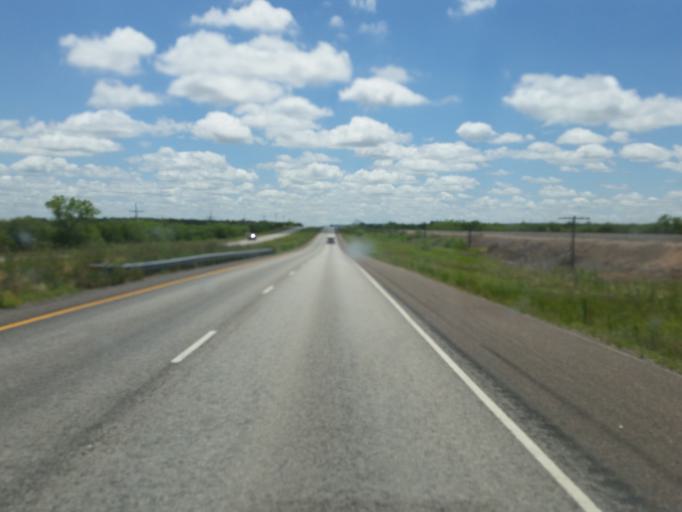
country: US
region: Texas
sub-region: Garza County
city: Post
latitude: 33.0358
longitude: -101.1956
